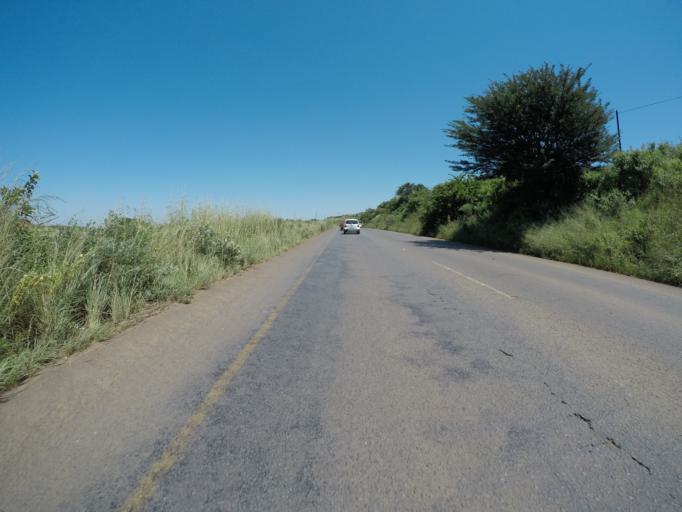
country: ZA
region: KwaZulu-Natal
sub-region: uThungulu District Municipality
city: Empangeni
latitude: -28.7532
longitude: 31.8761
